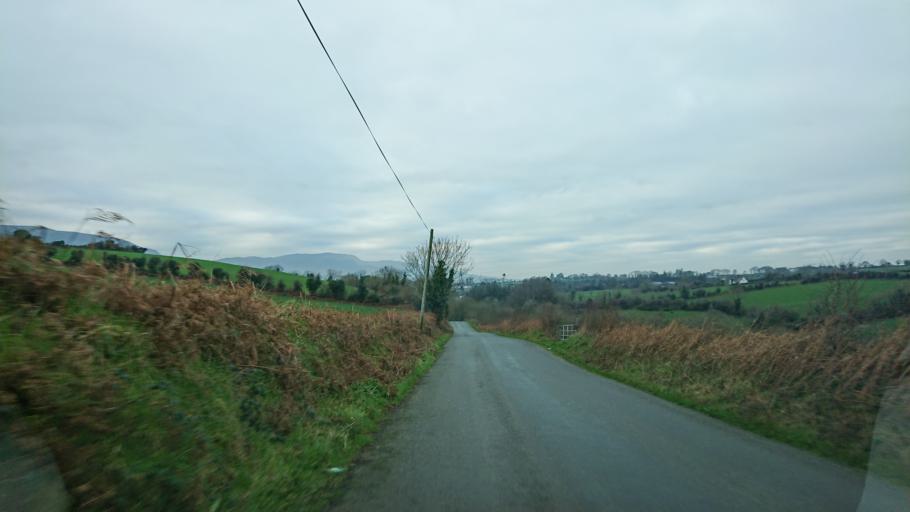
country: IE
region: Munster
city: Carrick-on-Suir
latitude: 52.2779
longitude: -7.4303
